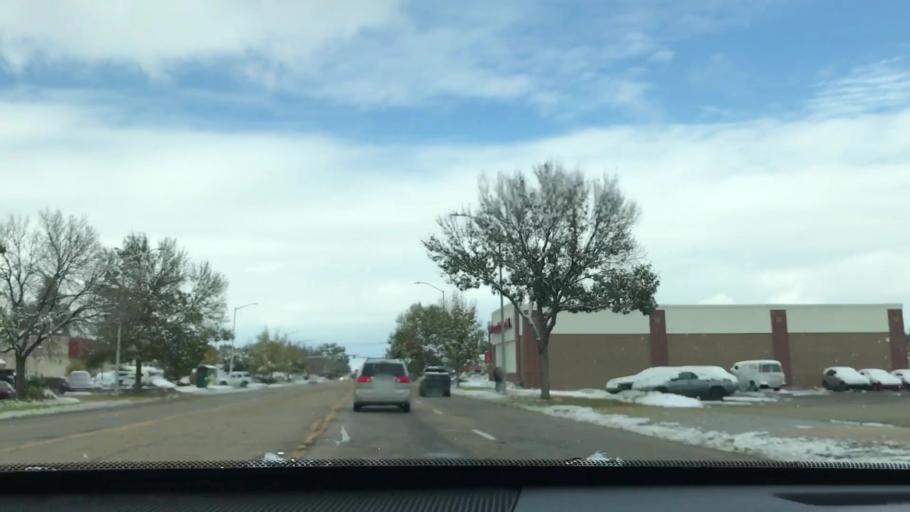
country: US
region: Colorado
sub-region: Boulder County
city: Longmont
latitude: 40.1827
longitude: -105.1023
